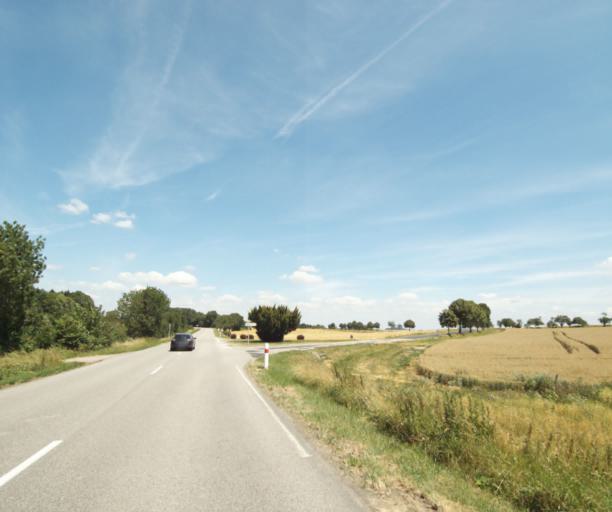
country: FR
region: Lorraine
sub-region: Departement de Meurthe-et-Moselle
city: Einville-au-Jard
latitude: 48.6259
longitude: 6.4889
